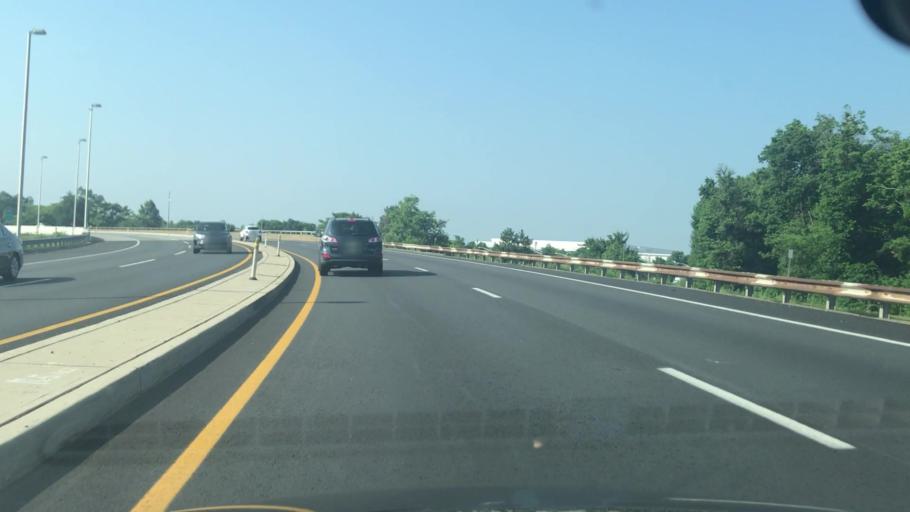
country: US
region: New Jersey
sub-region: Middlesex County
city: Metuchen
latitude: 40.5269
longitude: -74.3430
